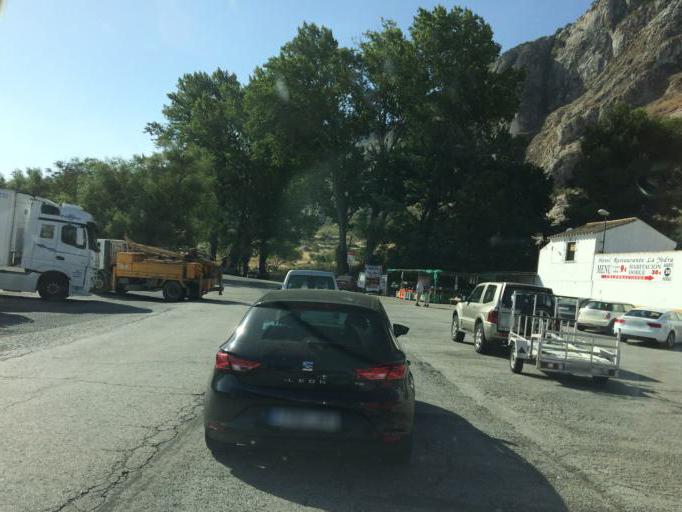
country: ES
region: Andalusia
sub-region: Provincia de Malaga
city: Casabermeja
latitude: 36.9818
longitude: -4.4594
